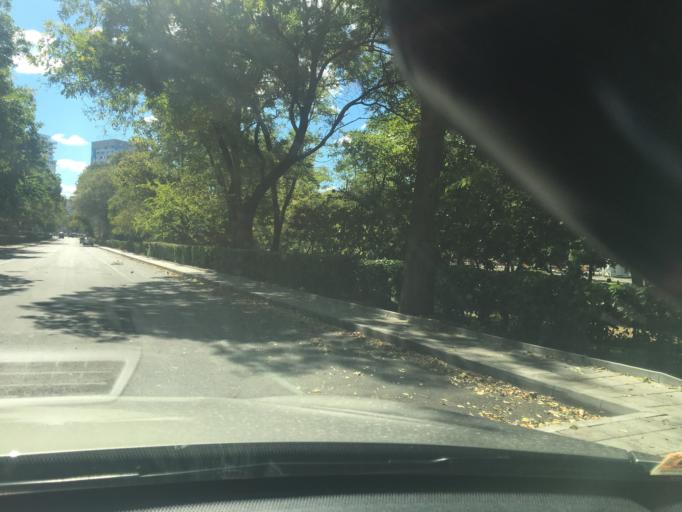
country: BG
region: Burgas
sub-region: Obshtina Burgas
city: Burgas
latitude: 42.5080
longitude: 27.4827
